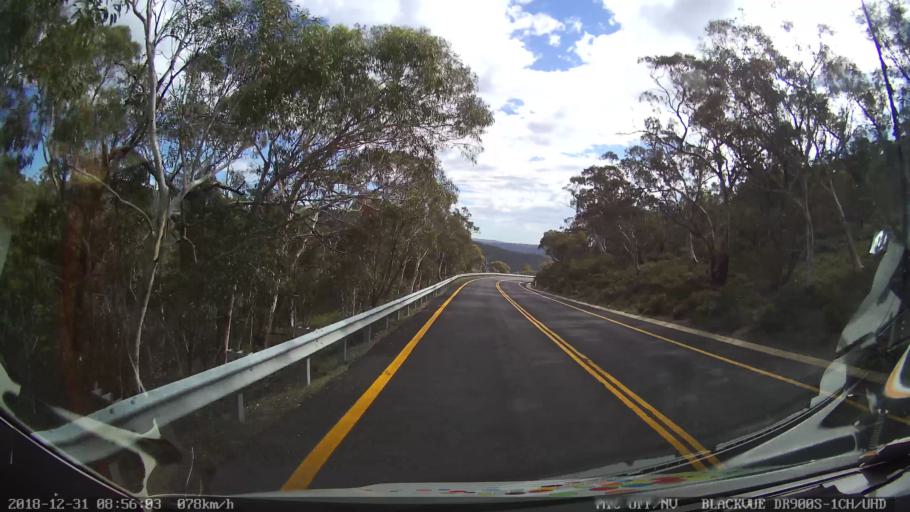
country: AU
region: New South Wales
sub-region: Snowy River
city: Jindabyne
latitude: -36.3435
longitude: 148.5755
